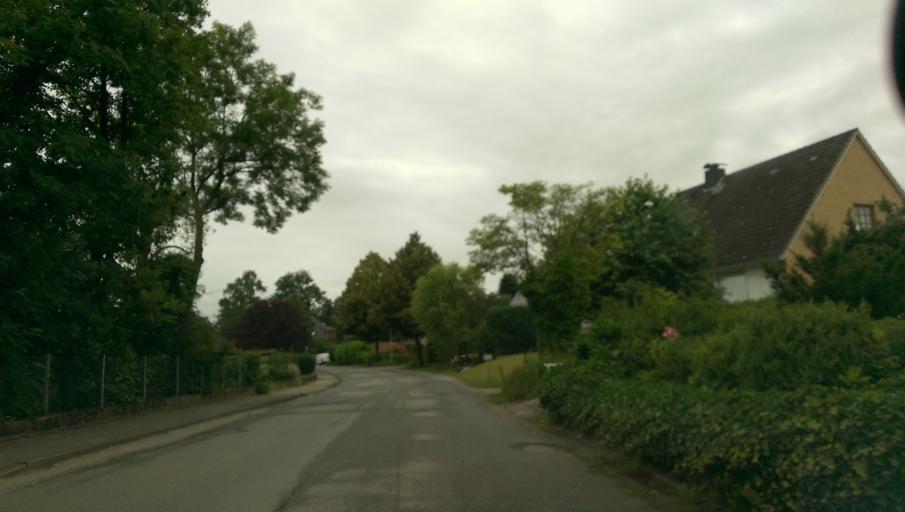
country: DE
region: Schleswig-Holstein
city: Ratekau
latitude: 53.9849
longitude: 10.7110
